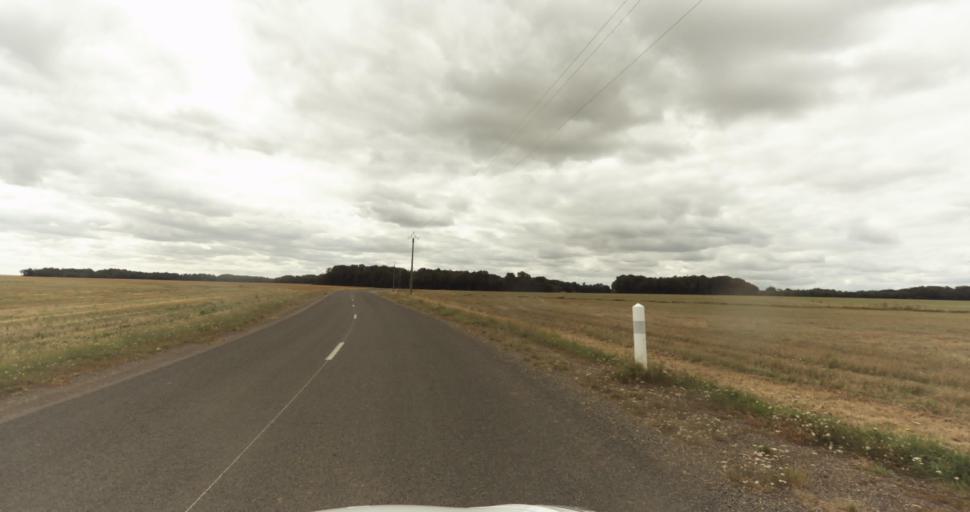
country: FR
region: Haute-Normandie
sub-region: Departement de l'Eure
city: La Madeleine-de-Nonancourt
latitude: 48.8249
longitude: 1.2250
